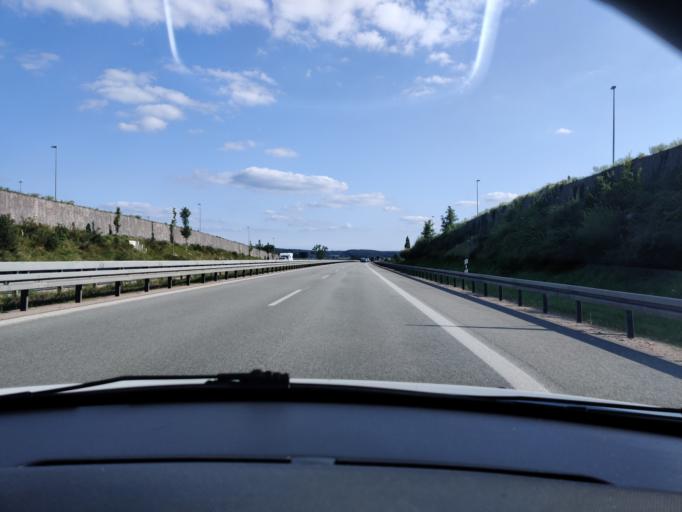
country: DE
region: Bavaria
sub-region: Upper Palatinate
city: Pfreimd
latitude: 49.4759
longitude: 12.1919
